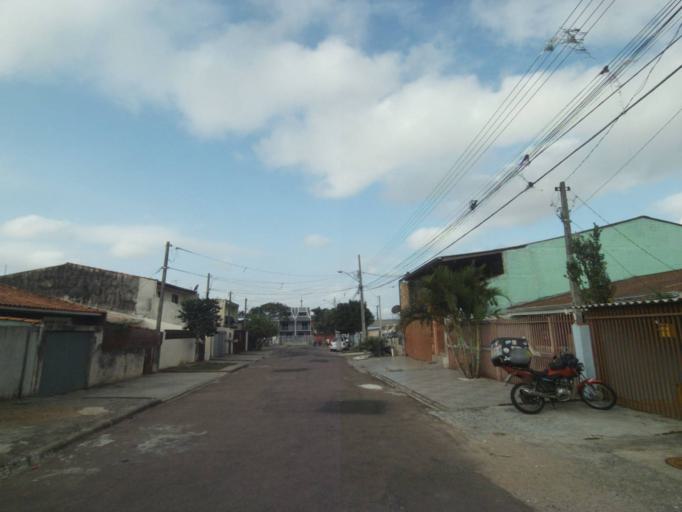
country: BR
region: Parana
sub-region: Sao Jose Dos Pinhais
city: Sao Jose dos Pinhais
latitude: -25.5455
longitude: -49.2619
